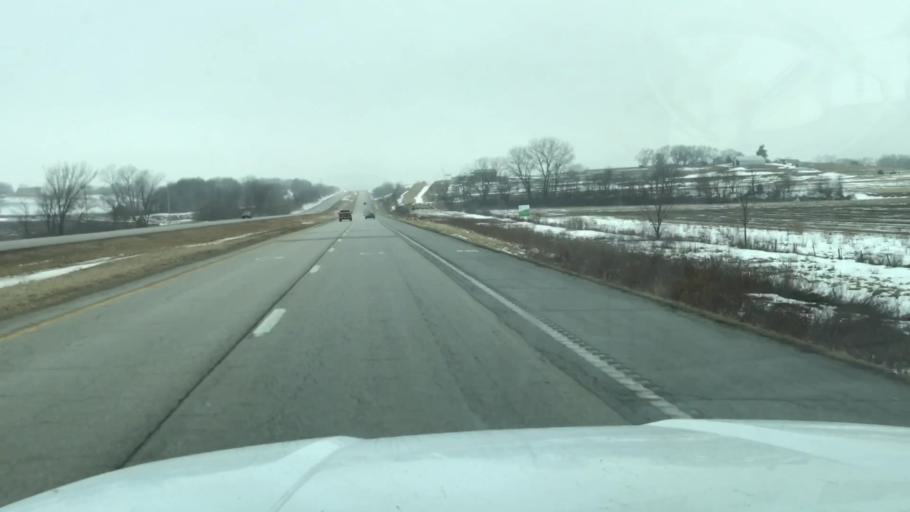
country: US
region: Missouri
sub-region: Clinton County
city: Gower
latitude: 39.7477
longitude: -94.6663
